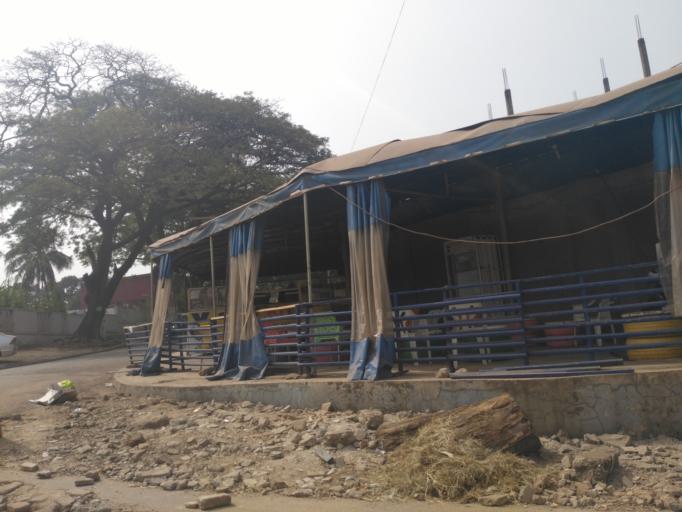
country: GH
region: Ashanti
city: Kumasi
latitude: 6.6798
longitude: -1.6007
